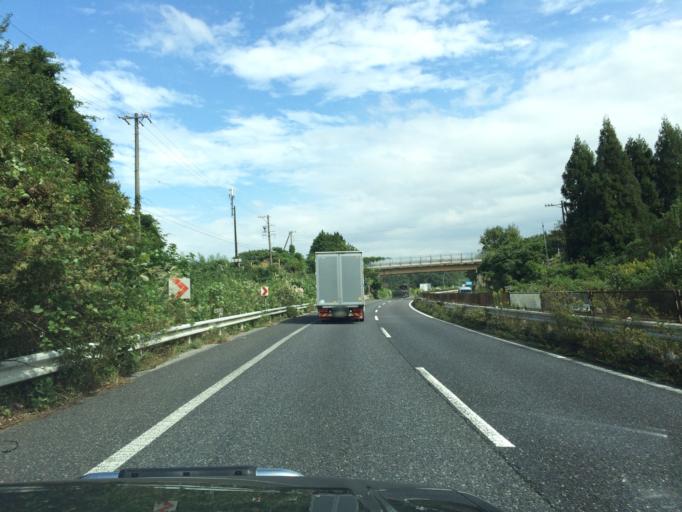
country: JP
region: Mie
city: Ueno-ebisumachi
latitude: 34.7018
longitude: 136.0657
